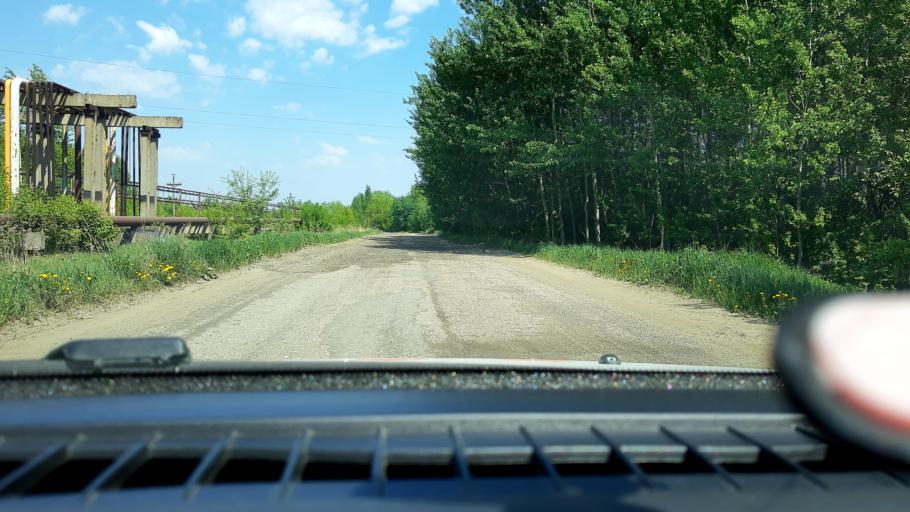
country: RU
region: Nizjnij Novgorod
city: Kstovo
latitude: 56.1288
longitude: 44.1272
